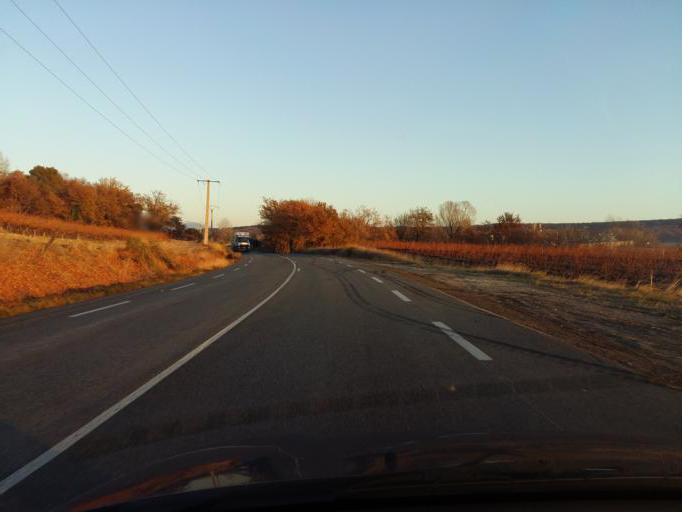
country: FR
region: Rhone-Alpes
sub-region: Departement de la Drome
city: Montsegur-sur-Lauzon
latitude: 44.4207
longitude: 4.8347
